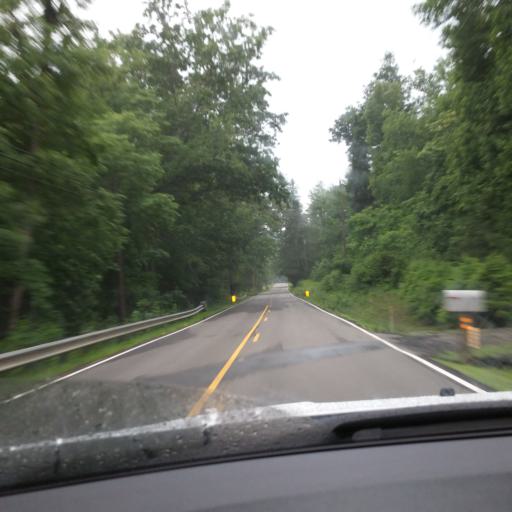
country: US
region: North Carolina
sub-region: Yancey County
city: Burnsville
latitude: 35.8236
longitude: -82.1898
